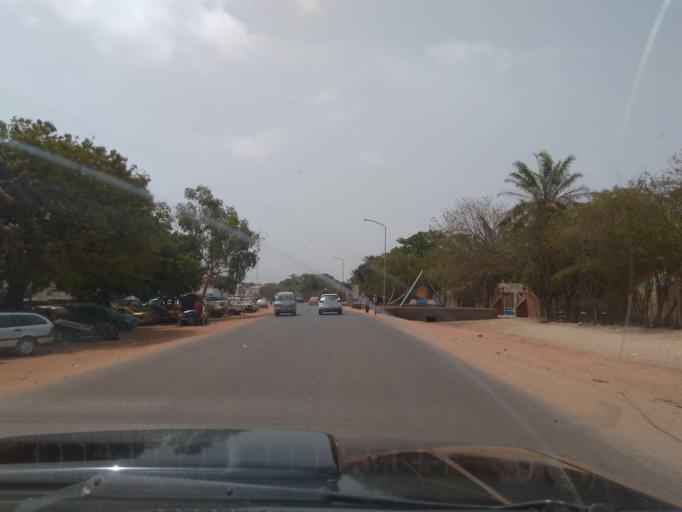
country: GM
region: Western
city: Sukuta
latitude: 13.4392
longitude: -16.7023
